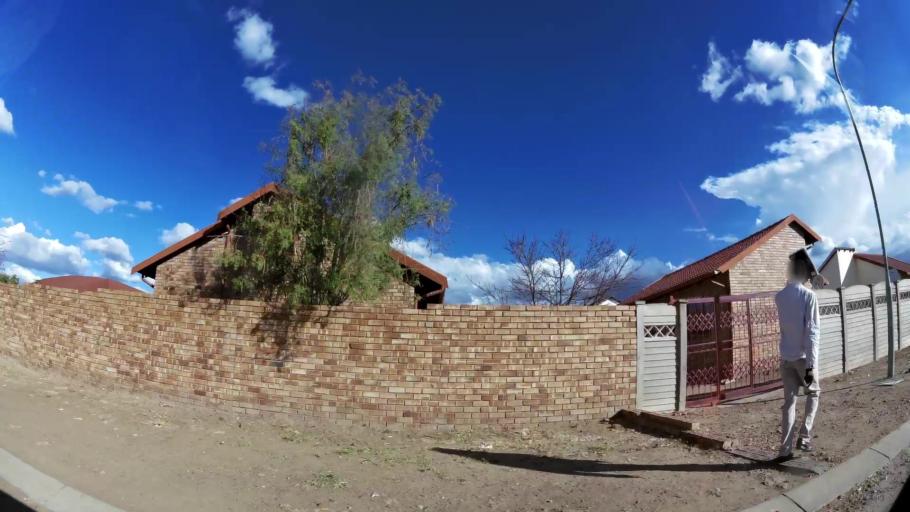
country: ZA
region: Limpopo
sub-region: Capricorn District Municipality
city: Polokwane
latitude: -23.9377
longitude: 29.4437
